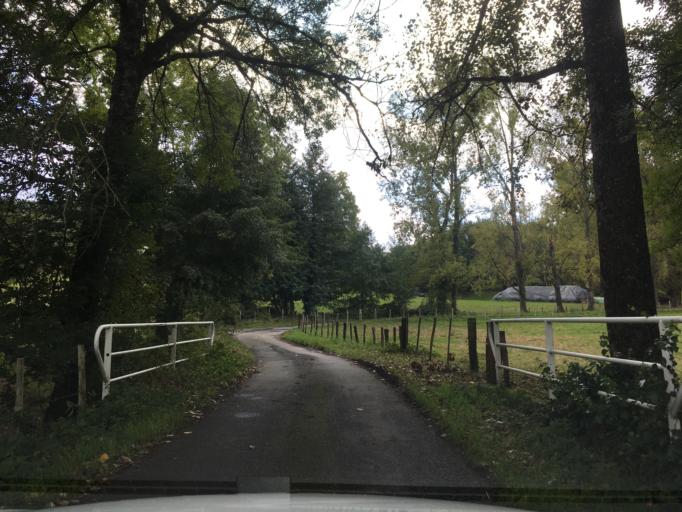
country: FR
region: Limousin
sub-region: Departement de la Correze
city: Brive-la-Gaillarde
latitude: 45.1214
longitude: 1.5447
